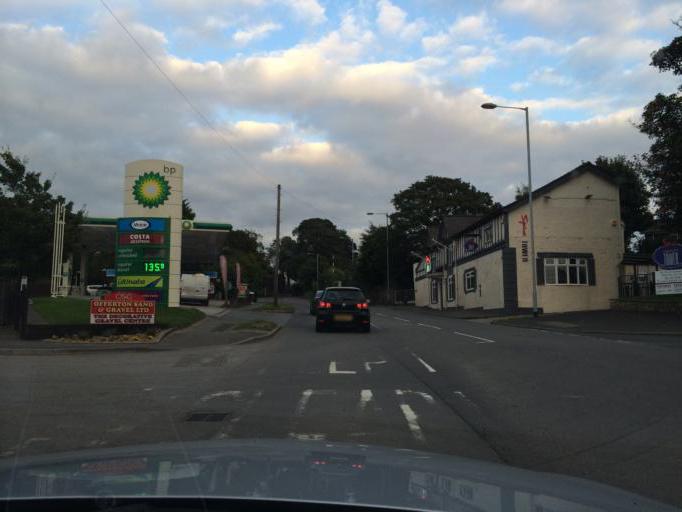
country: GB
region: England
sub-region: Borough of Stockport
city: Hazel Grove
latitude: 53.3958
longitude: -2.1102
